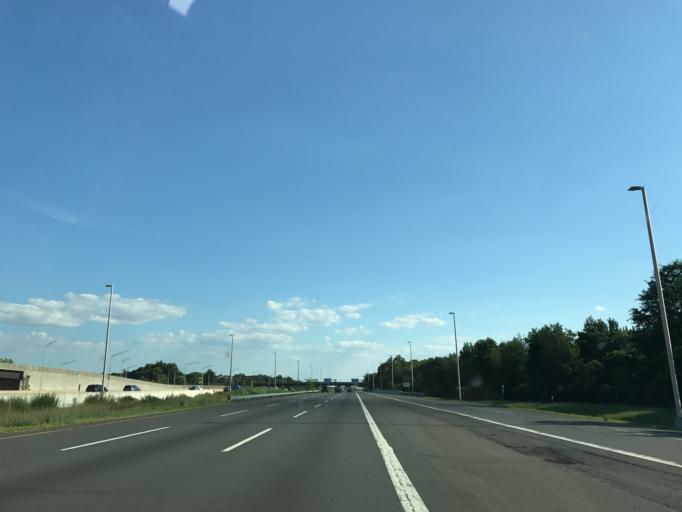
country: US
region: New Jersey
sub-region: Middlesex County
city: Rossmoor
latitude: 40.3493
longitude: -74.4748
